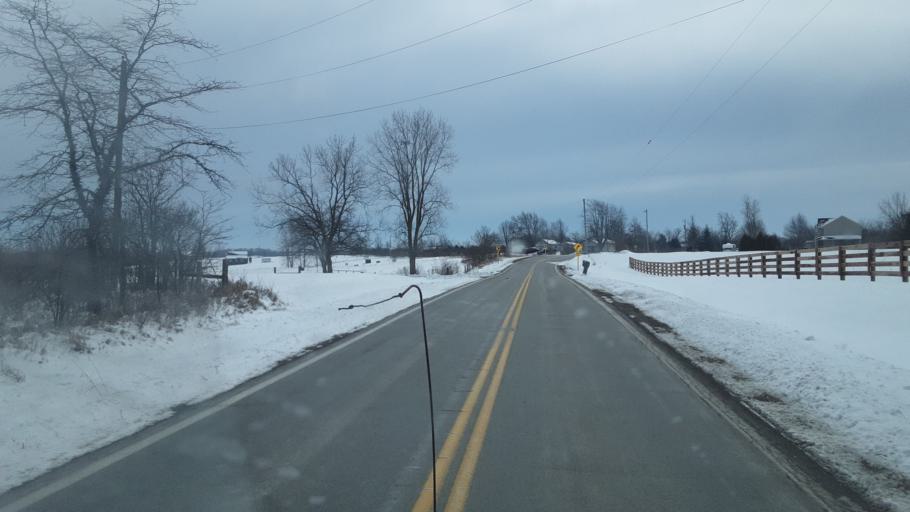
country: US
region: Ohio
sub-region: Madison County
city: Choctaw Lake
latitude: 39.9891
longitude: -83.4980
